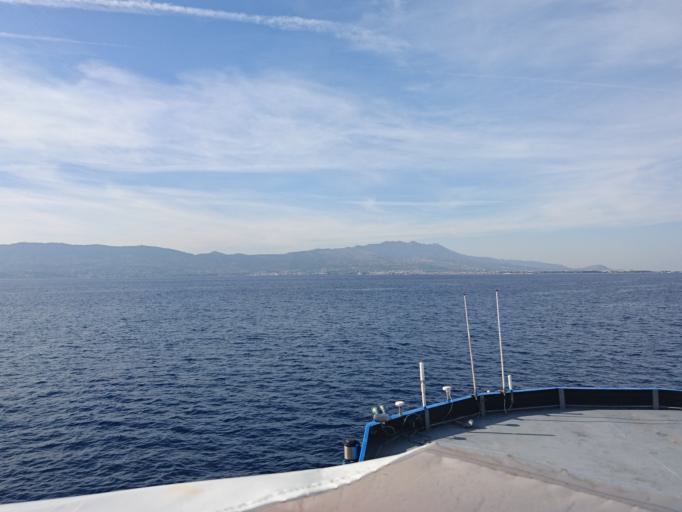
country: GR
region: South Aegean
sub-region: Nomos Dodekanisou
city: Kos
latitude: 36.9338
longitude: 27.3281
